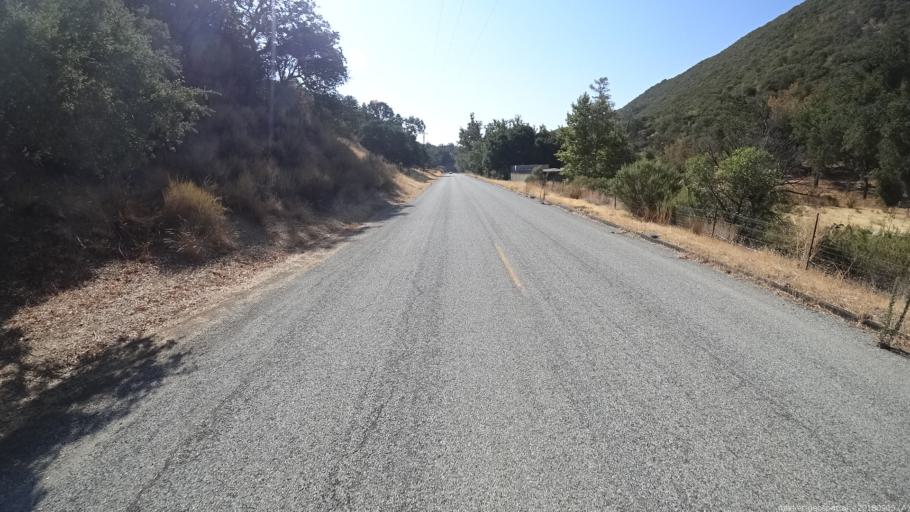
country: US
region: California
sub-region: Monterey County
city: Soledad
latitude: 36.3150
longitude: -121.4848
